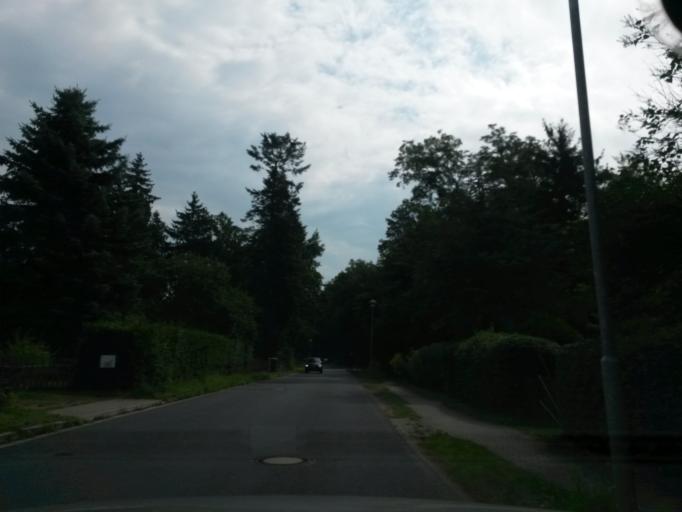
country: DE
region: Brandenburg
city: Chorin
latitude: 52.9009
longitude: 13.8836
